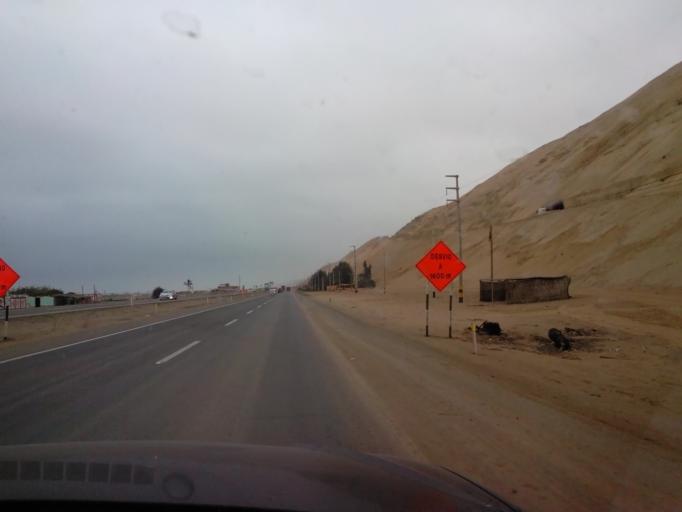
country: PE
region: Ica
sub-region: Provincia de Chincha
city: San Pedro
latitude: -13.3384
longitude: -76.2322
